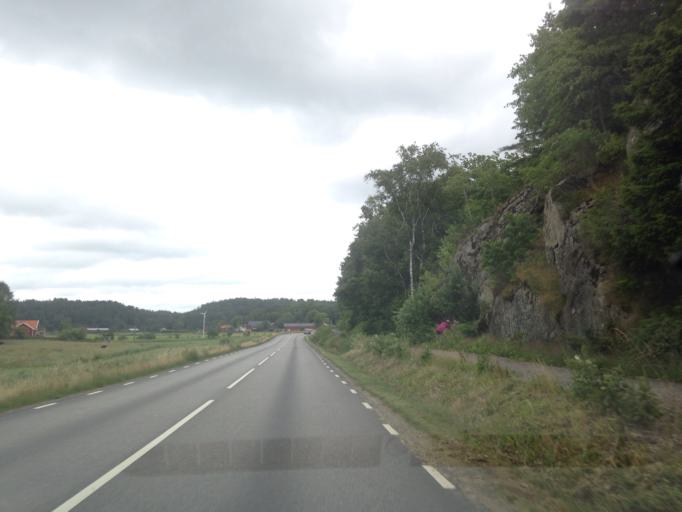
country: SE
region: Vaestra Goetaland
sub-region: Kungalvs Kommun
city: Kode
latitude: 57.8538
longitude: 11.8103
